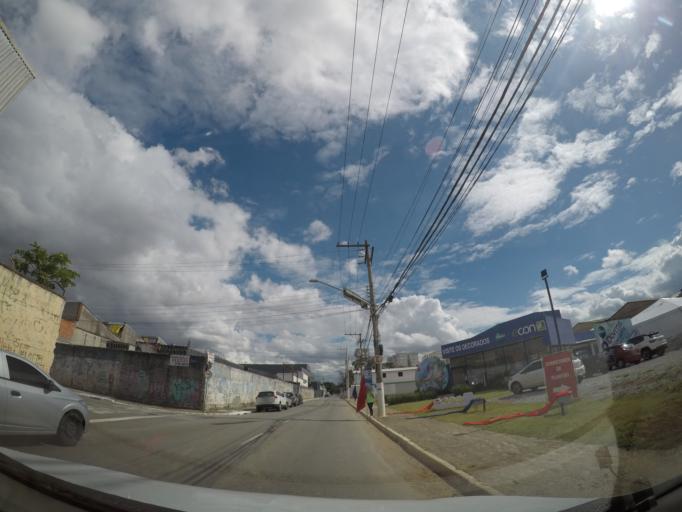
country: BR
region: Sao Paulo
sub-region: Guarulhos
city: Guarulhos
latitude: -23.4871
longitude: -46.5536
